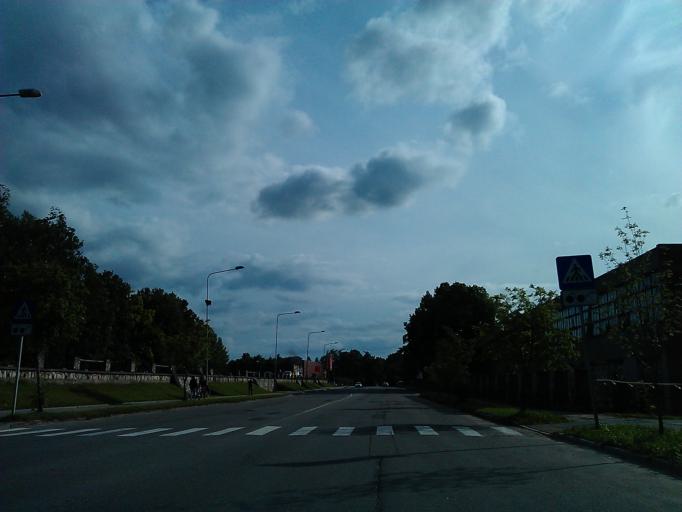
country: LV
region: Cesu Rajons
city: Cesis
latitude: 57.3118
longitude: 25.2794
